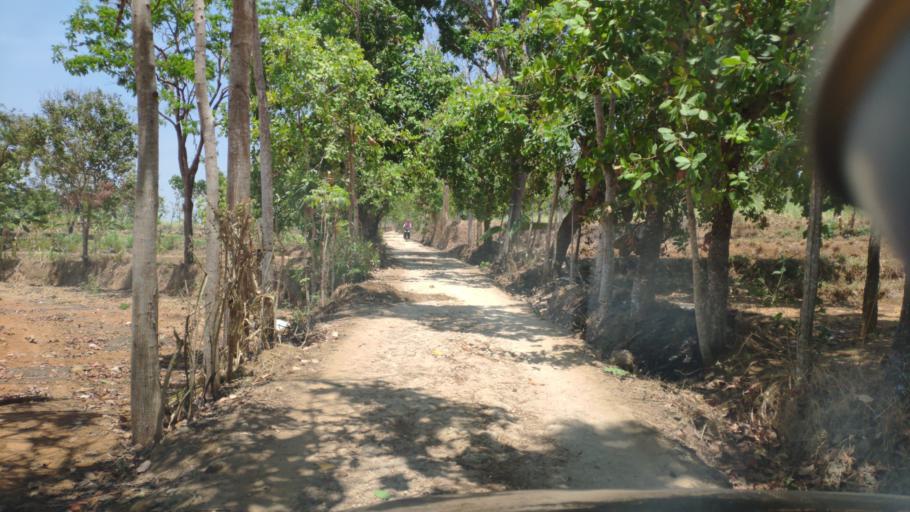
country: ID
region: Central Java
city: Ngapus
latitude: -6.9486
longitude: 111.1787
